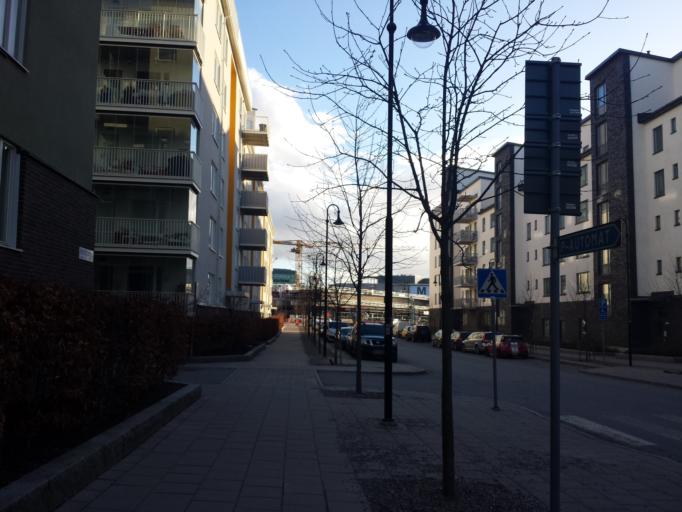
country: SE
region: Stockholm
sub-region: Solna Kommun
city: Solna
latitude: 59.3747
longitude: 18.0111
